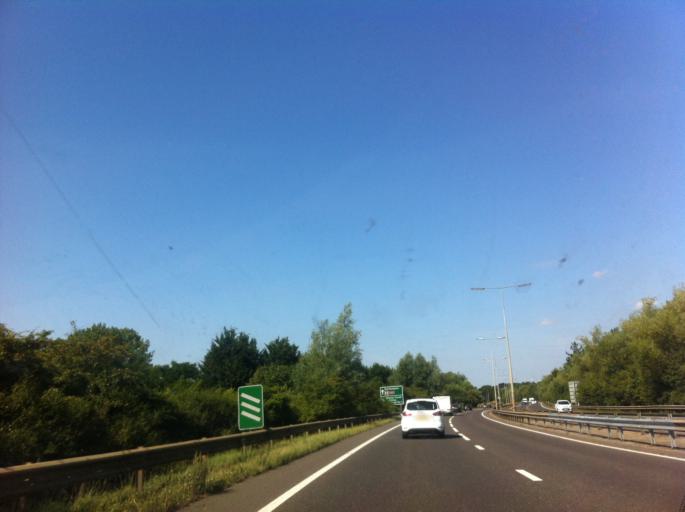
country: GB
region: England
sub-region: Northamptonshire
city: Earls Barton
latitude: 52.2484
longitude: -0.8148
